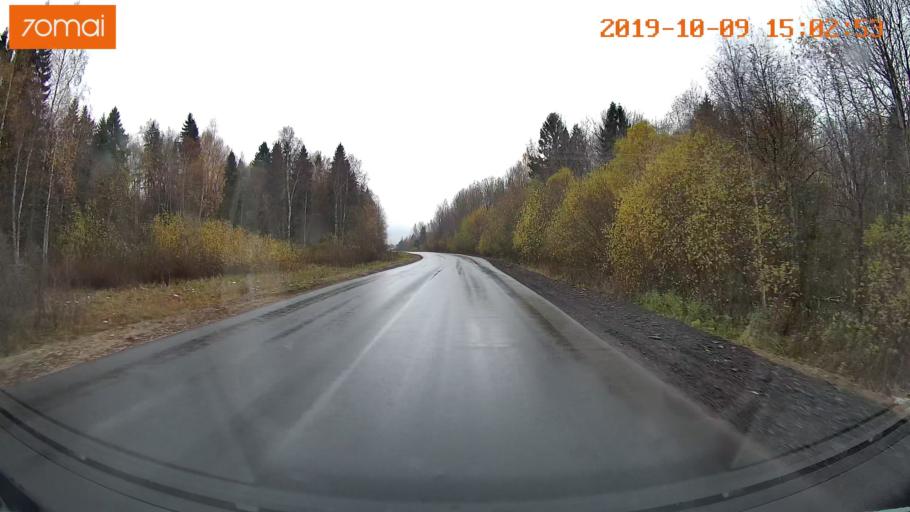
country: RU
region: Kostroma
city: Chistyye Bory
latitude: 58.2787
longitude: 41.6767
